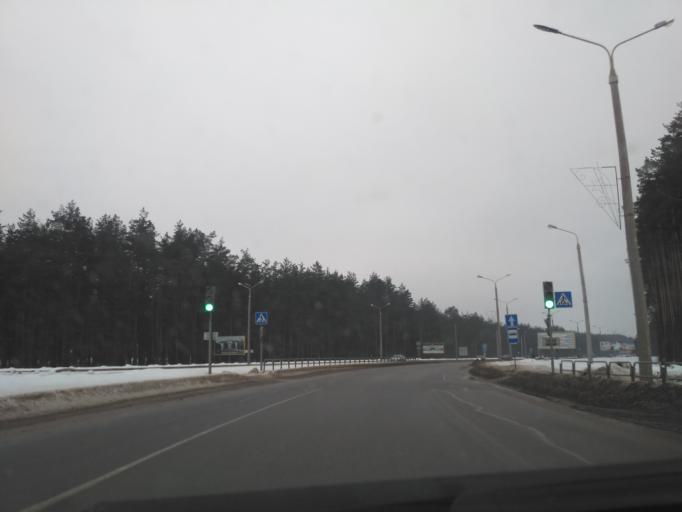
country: BY
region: Minsk
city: Horad Barysaw
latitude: 54.1958
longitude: 28.4685
